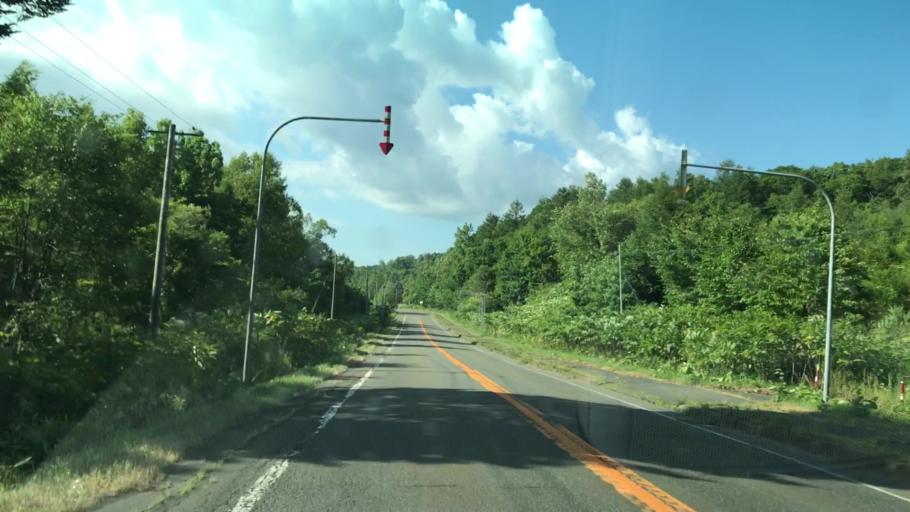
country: JP
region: Hokkaido
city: Shimo-furano
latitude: 42.8935
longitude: 142.4305
